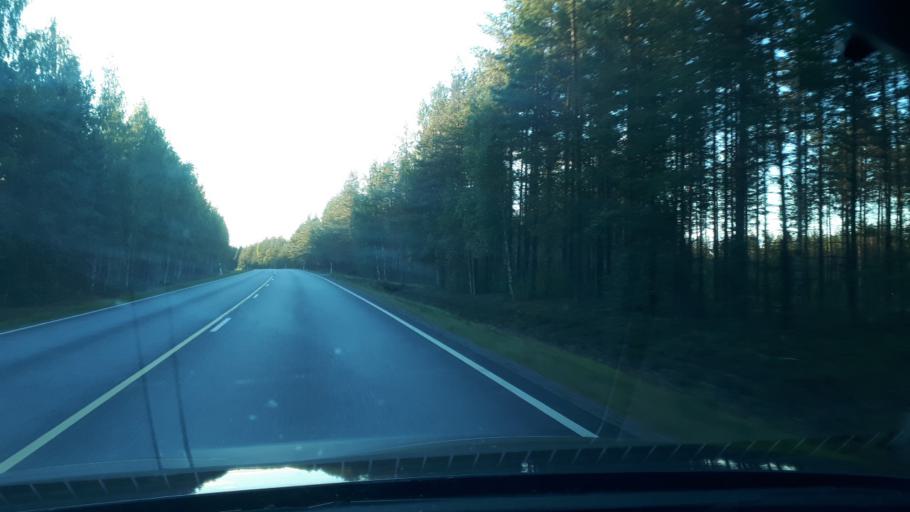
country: FI
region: Northern Ostrobothnia
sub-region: Haapavesi-Siikalatva
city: Pyhaentae
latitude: 64.1293
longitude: 26.2795
